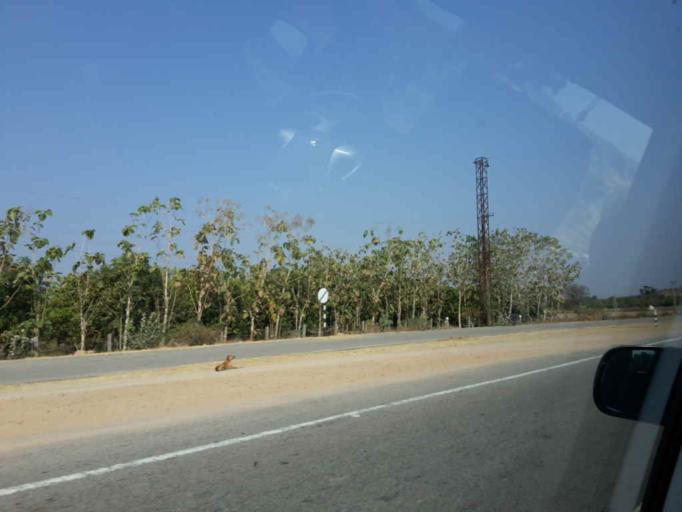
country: IN
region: Telangana
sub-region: Nizamabad District
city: Nizamabad
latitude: 18.7056
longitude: 78.2616
